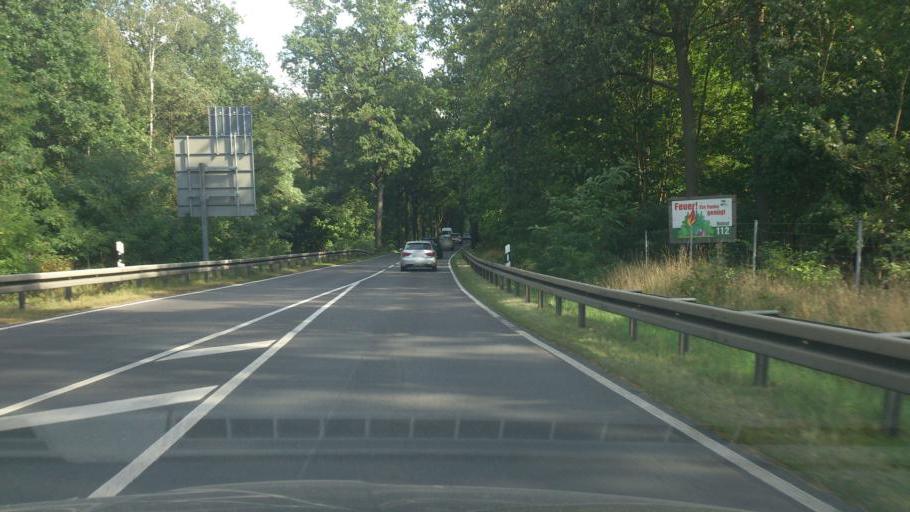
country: DE
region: Berlin
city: Wannsee
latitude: 52.3516
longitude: 13.1438
